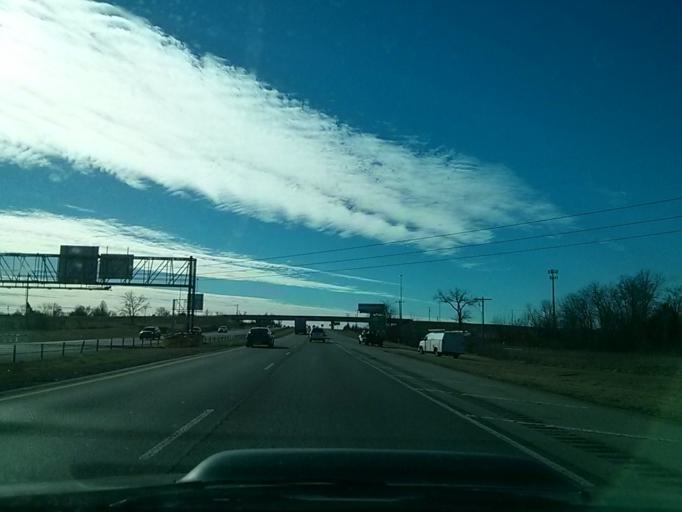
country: US
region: Oklahoma
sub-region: Tulsa County
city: Jenks
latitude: 36.0071
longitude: -96.0118
